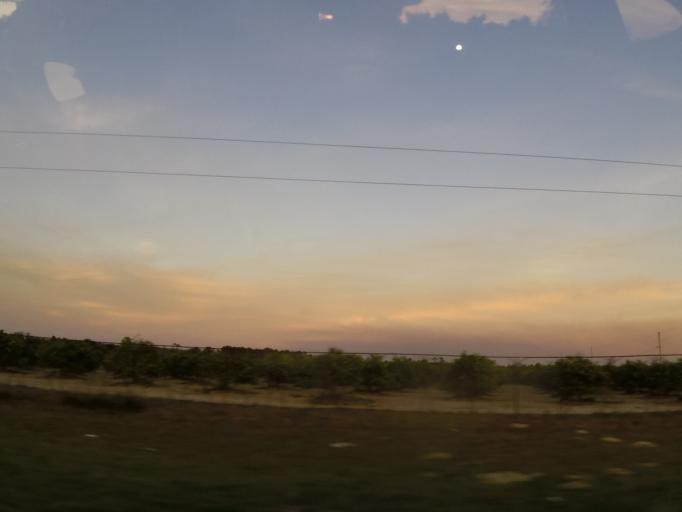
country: US
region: Florida
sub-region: Volusia County
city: De Leon Springs
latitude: 29.1599
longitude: -81.2960
